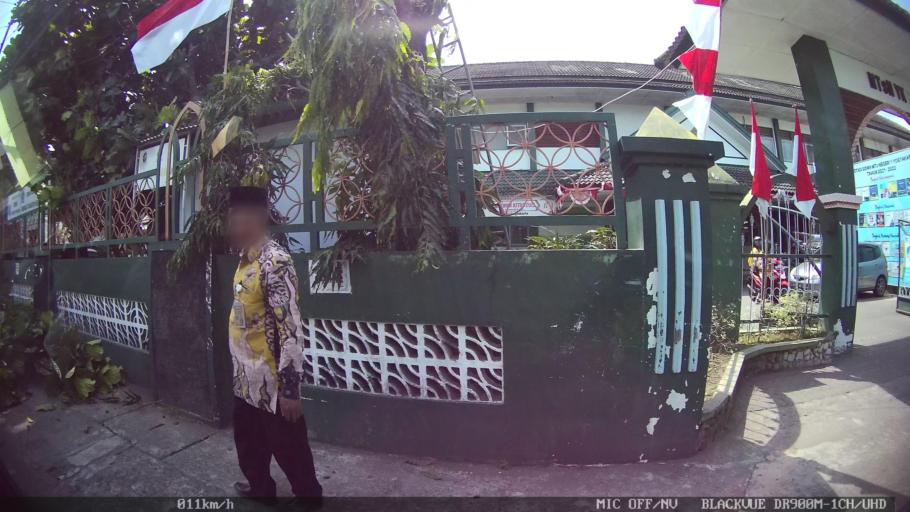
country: ID
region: Daerah Istimewa Yogyakarta
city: Sewon
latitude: -7.8311
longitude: 110.3883
